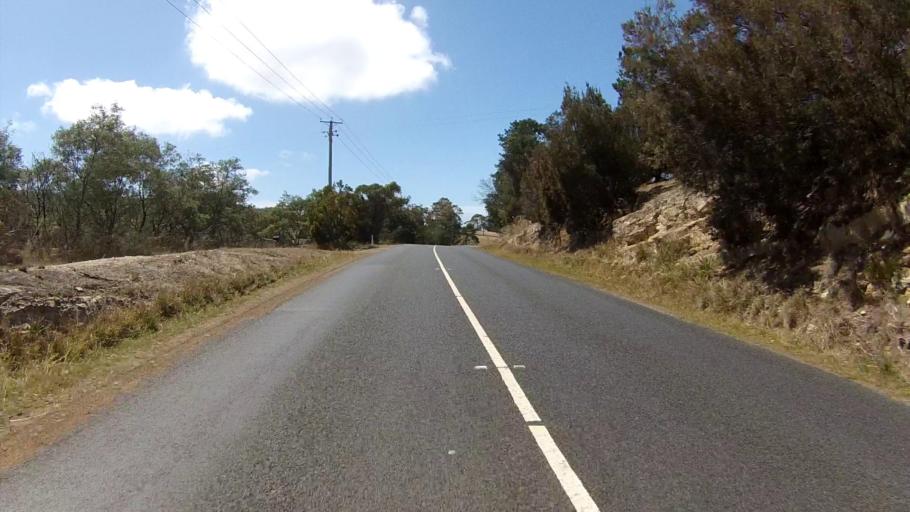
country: AU
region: Tasmania
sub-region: Clarence
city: Sandford
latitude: -42.9588
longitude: 147.4748
